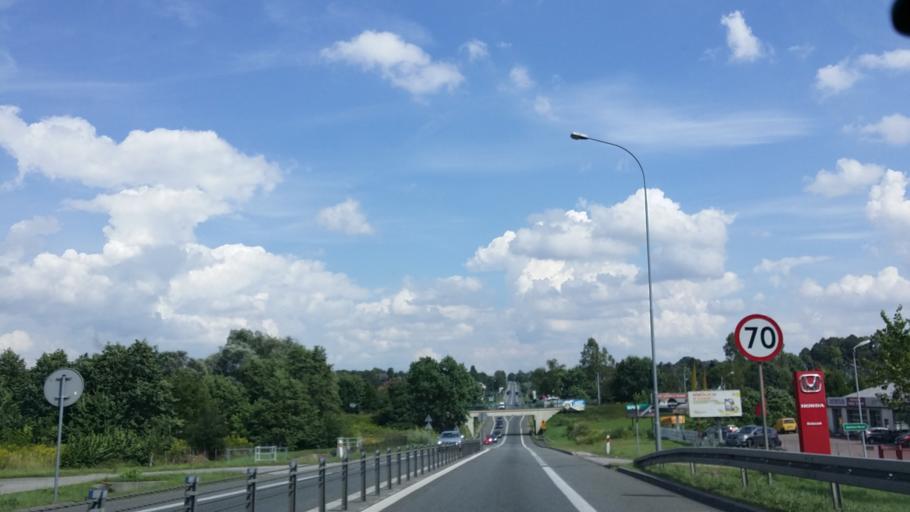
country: PL
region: Lesser Poland Voivodeship
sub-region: Powiat wielicki
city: Wieliczka
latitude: 49.9944
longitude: 20.0426
